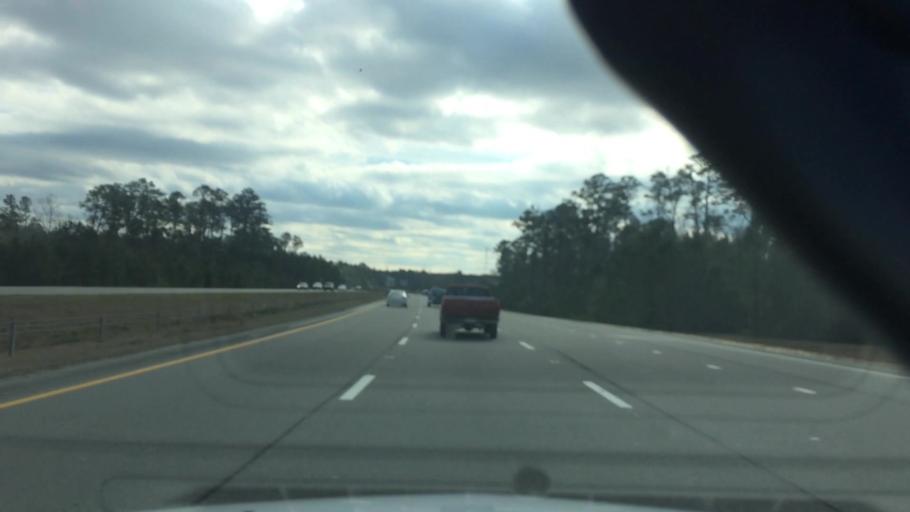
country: US
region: North Carolina
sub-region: Brunswick County
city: Leland
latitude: 34.1877
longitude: -78.0819
